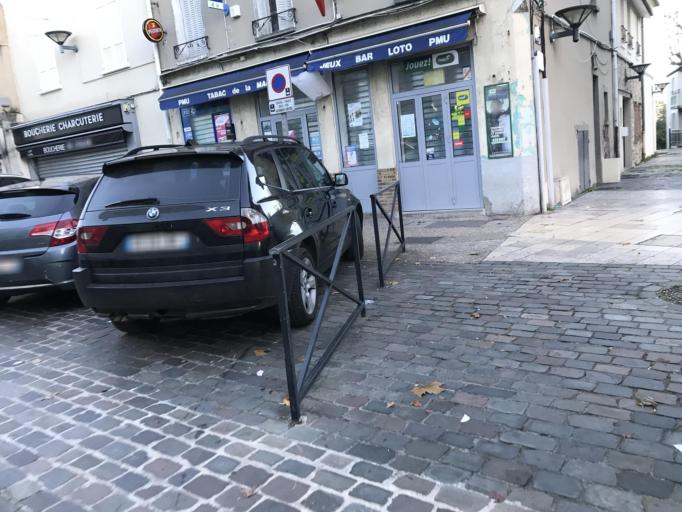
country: FR
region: Ile-de-France
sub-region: Departement de l'Essonne
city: Athis-Mons
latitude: 48.7083
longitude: 2.3889
